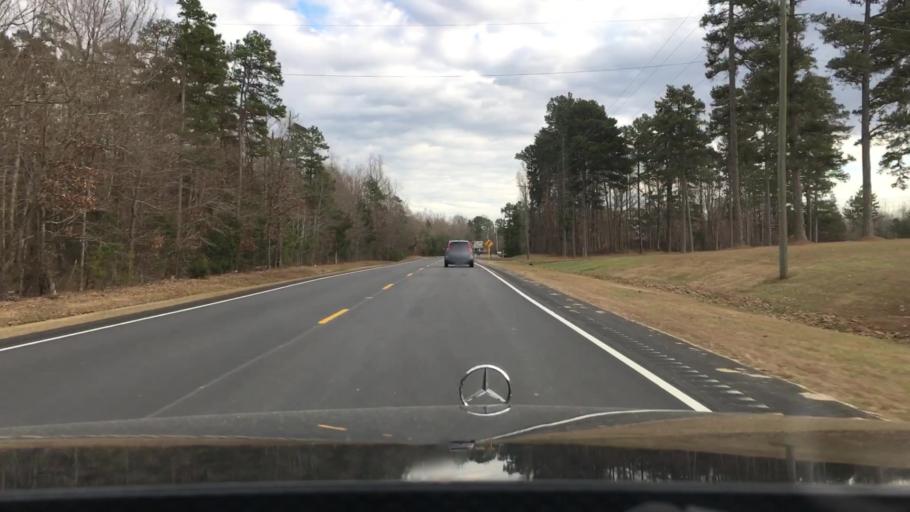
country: US
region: North Carolina
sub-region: Caswell County
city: Yanceyville
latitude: 36.2726
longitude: -79.2019
